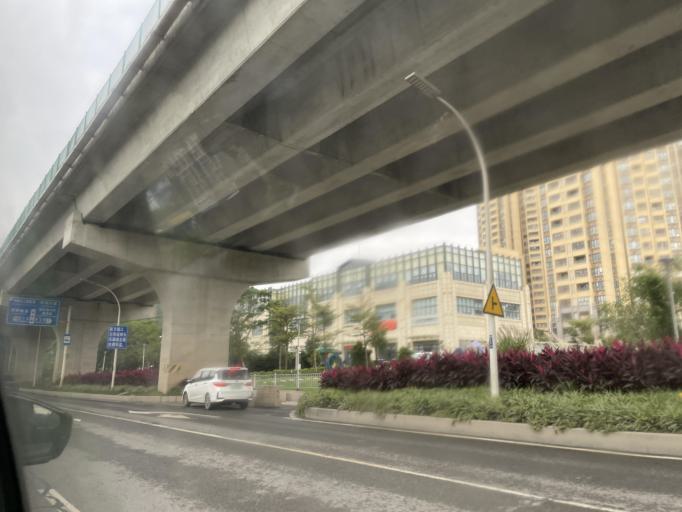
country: CN
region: Guangdong
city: Nanping
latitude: 22.1765
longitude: 113.4756
